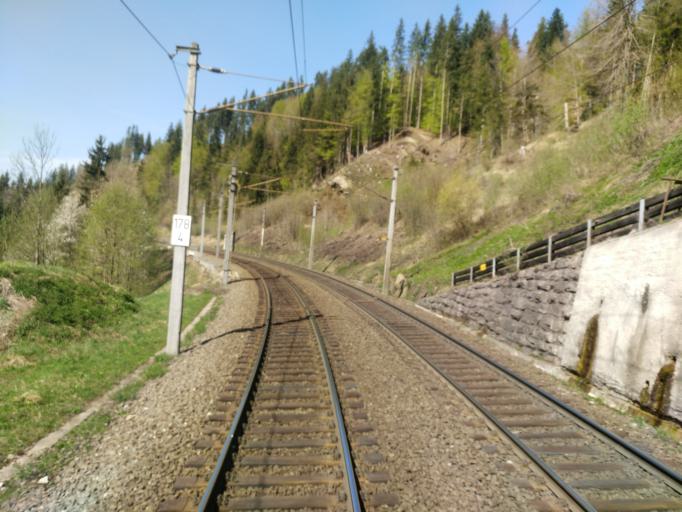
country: AT
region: Tyrol
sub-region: Politischer Bezirk Kitzbuhel
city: Westendorf
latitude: 47.4257
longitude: 12.1874
